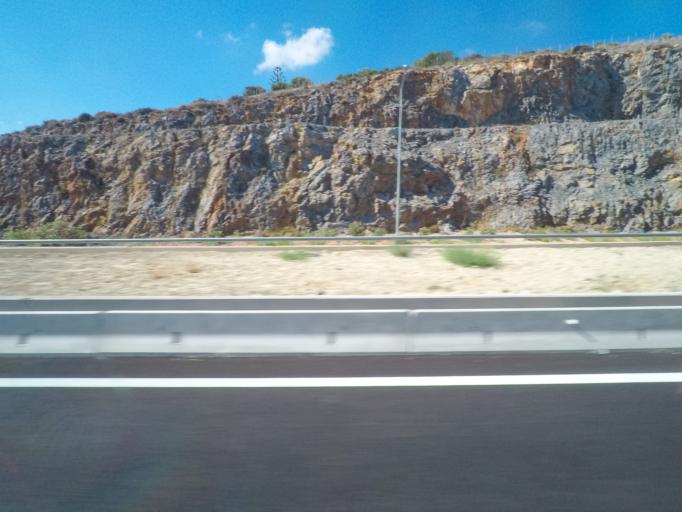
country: GR
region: Crete
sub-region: Nomos Irakleiou
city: Gournes
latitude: 35.3241
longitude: 25.2977
